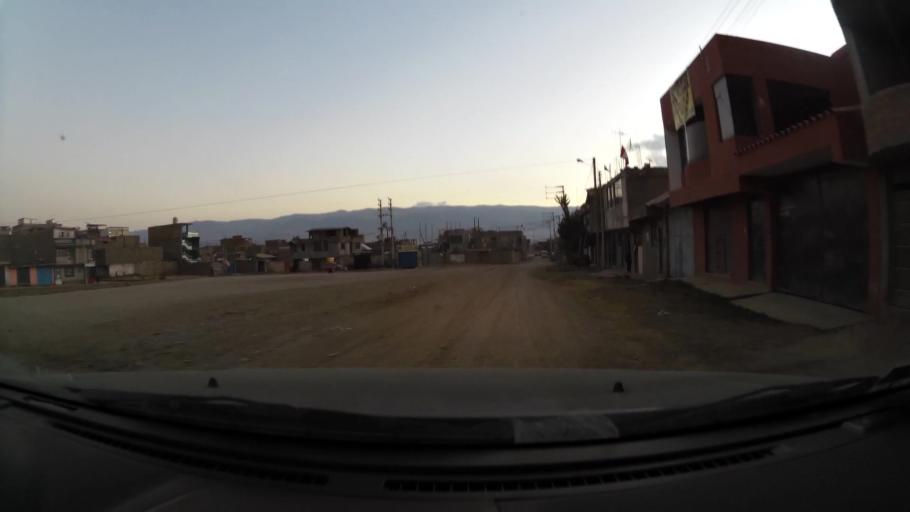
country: PE
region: Junin
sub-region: Provincia de Huancayo
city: El Tambo
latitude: -12.0599
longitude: -75.2318
